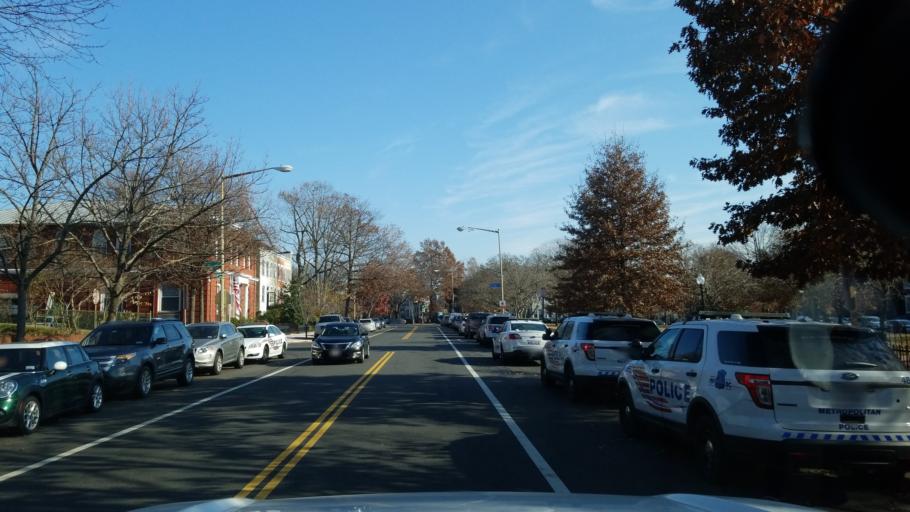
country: US
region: Washington, D.C.
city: Washington, D.C.
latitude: 38.8832
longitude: -77.0000
